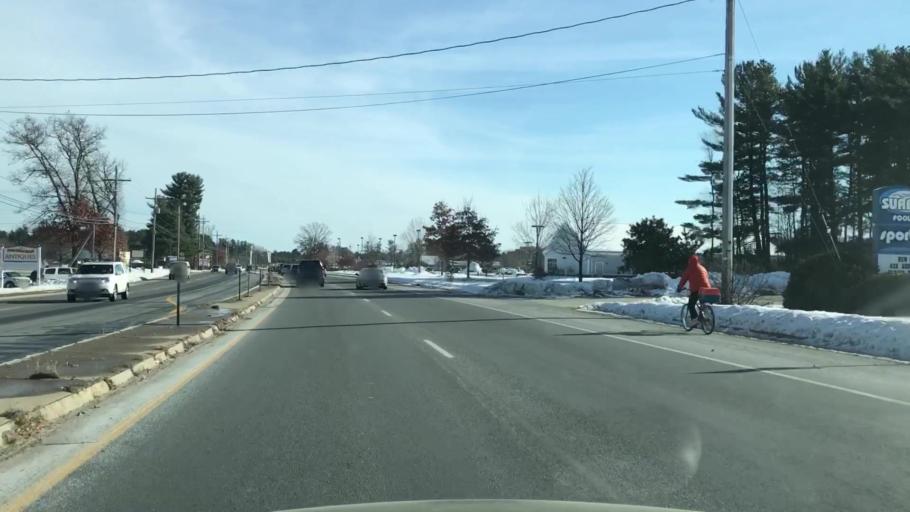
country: US
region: New Hampshire
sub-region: Hillsborough County
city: Hollis
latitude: 42.8088
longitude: -71.5724
